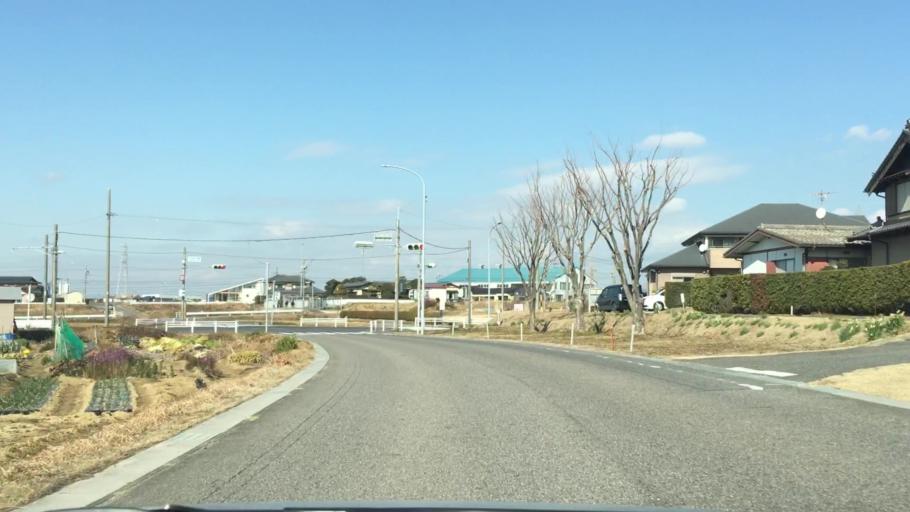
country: JP
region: Aichi
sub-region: Toyota-shi
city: Toyota
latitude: 35.0367
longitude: 137.1247
